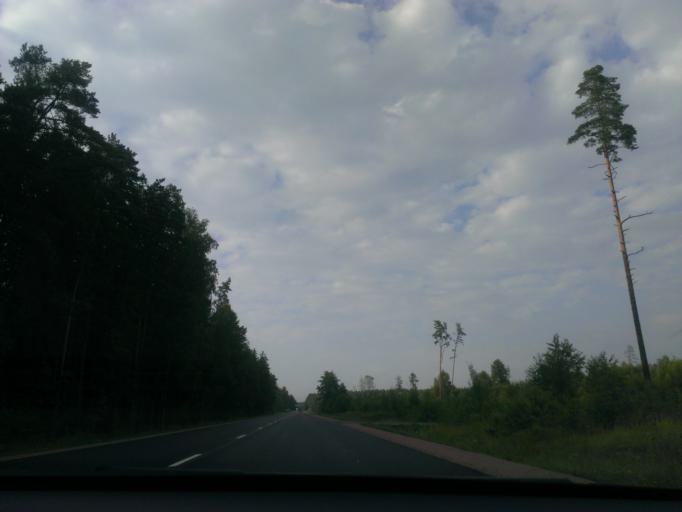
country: LV
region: Lecava
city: Iecava
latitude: 56.6981
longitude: 24.2432
